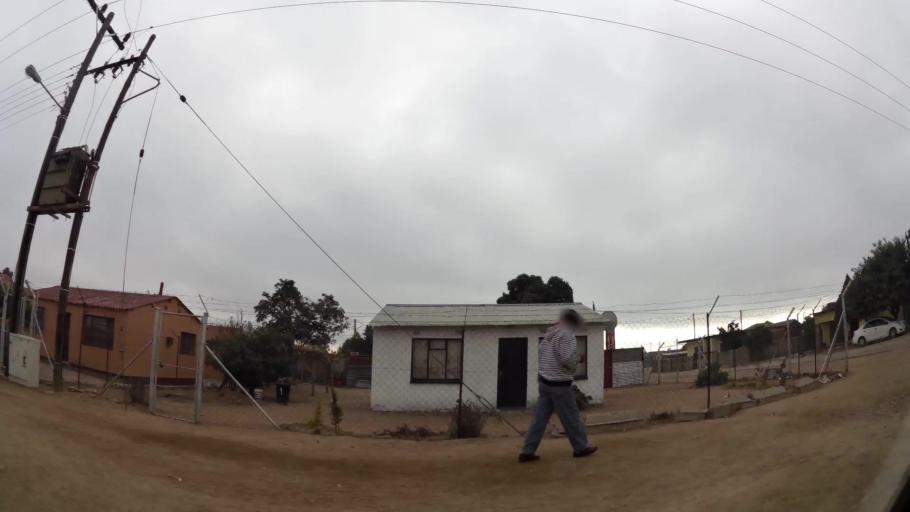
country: ZA
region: Limpopo
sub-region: Capricorn District Municipality
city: Polokwane
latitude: -23.8365
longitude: 29.3914
